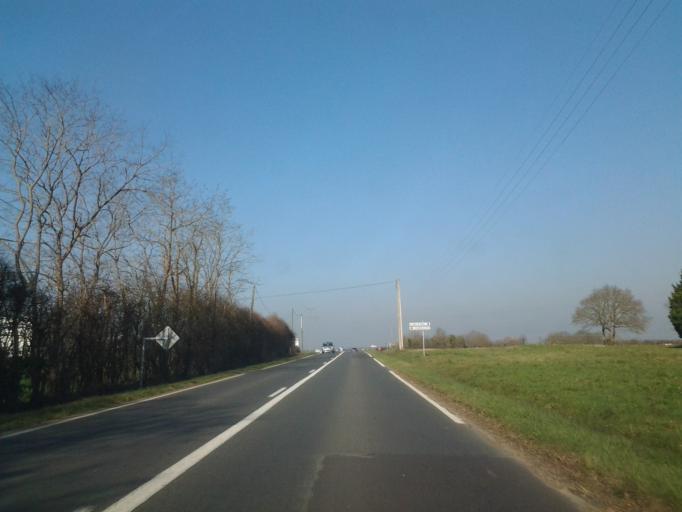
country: FR
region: Pays de la Loire
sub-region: Departement de la Vendee
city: Mache
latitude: 46.7876
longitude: -1.7007
